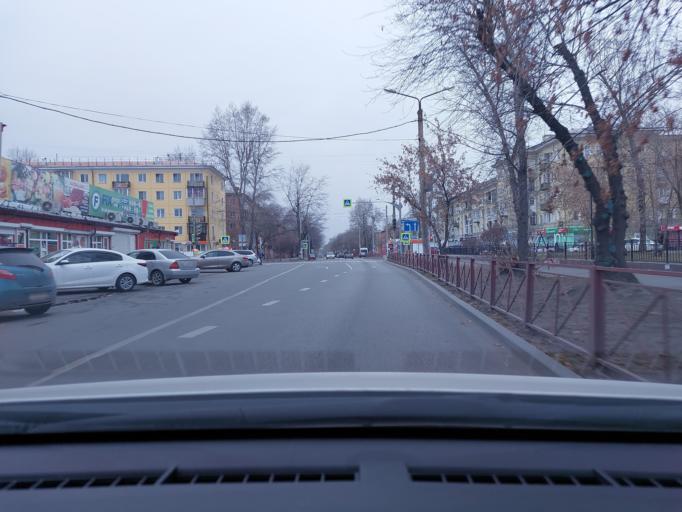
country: RU
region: Irkutsk
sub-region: Irkutskiy Rayon
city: Irkutsk
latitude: 52.3451
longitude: 104.2261
